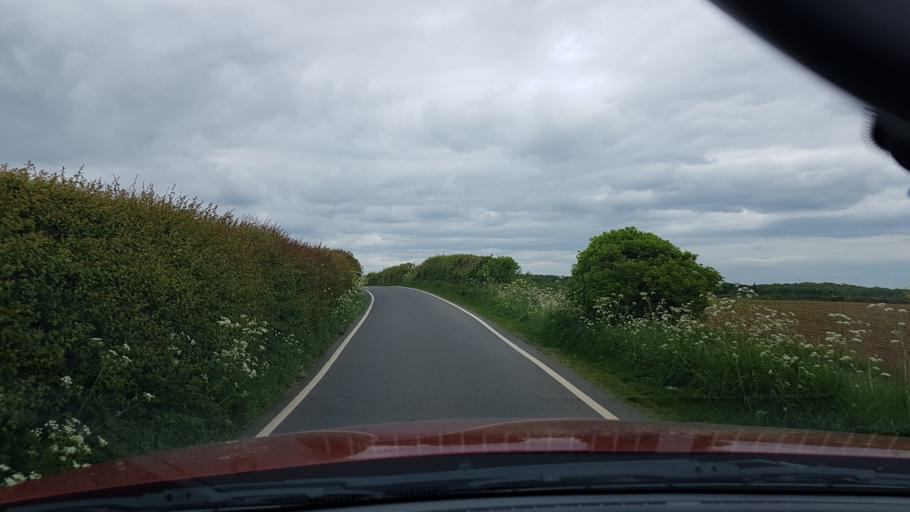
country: GB
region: England
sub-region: Rotherham
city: Maltby
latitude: 53.4034
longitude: -1.1958
